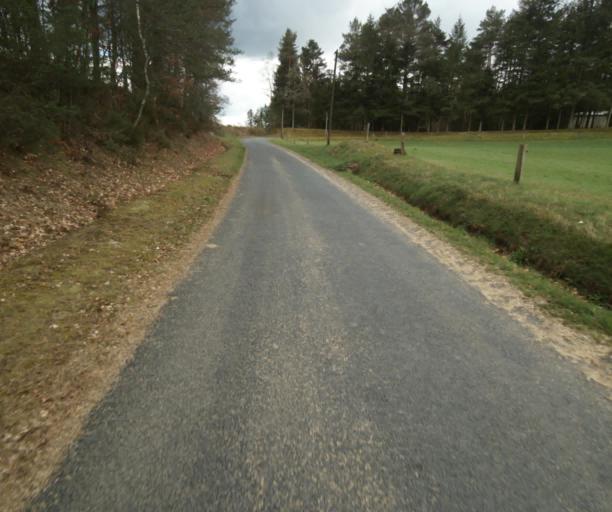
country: FR
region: Limousin
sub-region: Departement de la Correze
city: Correze
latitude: 45.2693
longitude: 1.9654
